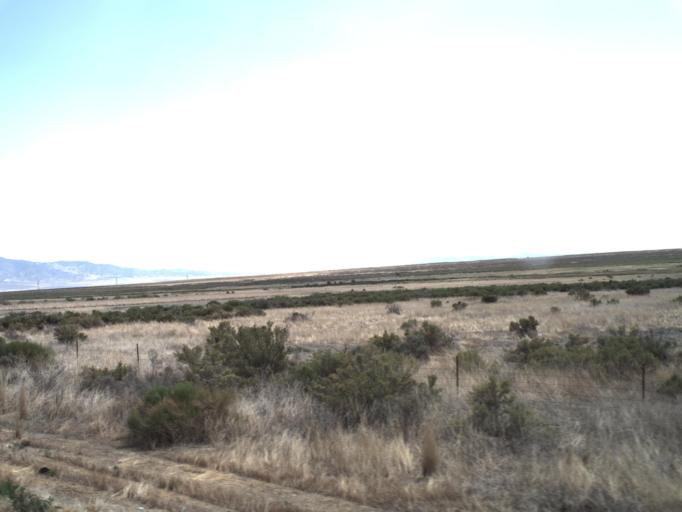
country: US
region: Utah
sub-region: Tooele County
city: Tooele
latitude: 40.1846
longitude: -112.4213
